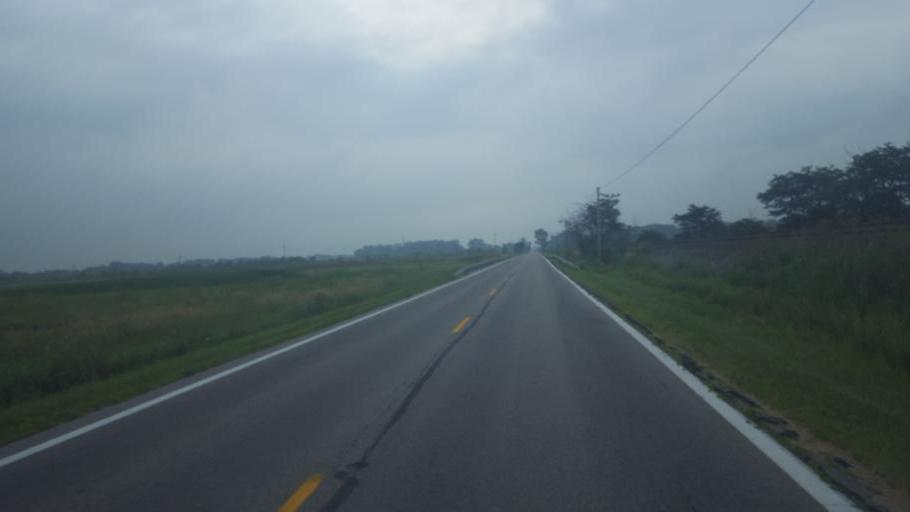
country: US
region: Ohio
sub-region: Marion County
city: Marion
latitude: 40.5861
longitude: -83.2087
